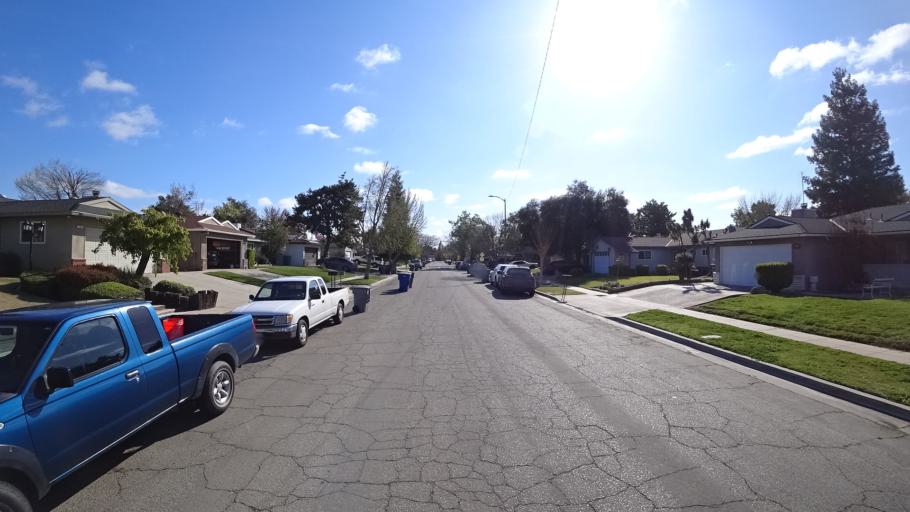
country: US
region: California
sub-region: Fresno County
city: West Park
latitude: 36.7960
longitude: -119.8792
